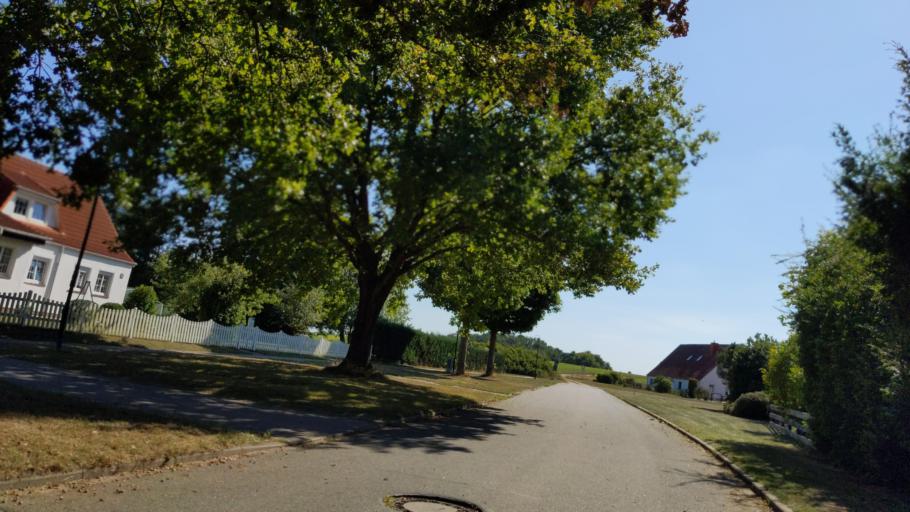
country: DE
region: Schleswig-Holstein
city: Gross Gronau
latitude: 53.8268
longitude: 10.8091
